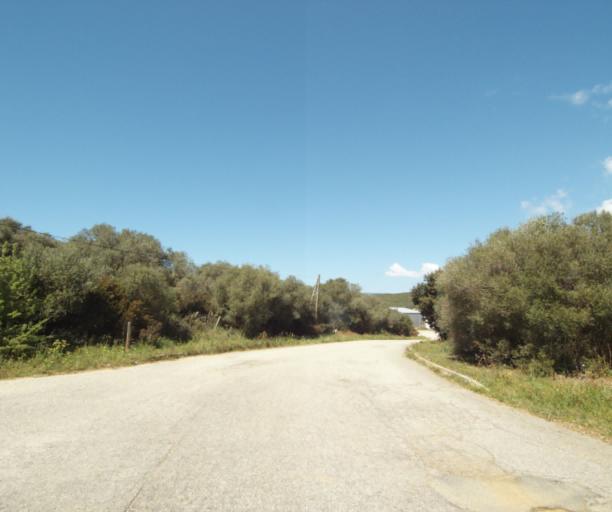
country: FR
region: Corsica
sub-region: Departement de la Corse-du-Sud
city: Propriano
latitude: 41.6578
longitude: 8.8939
